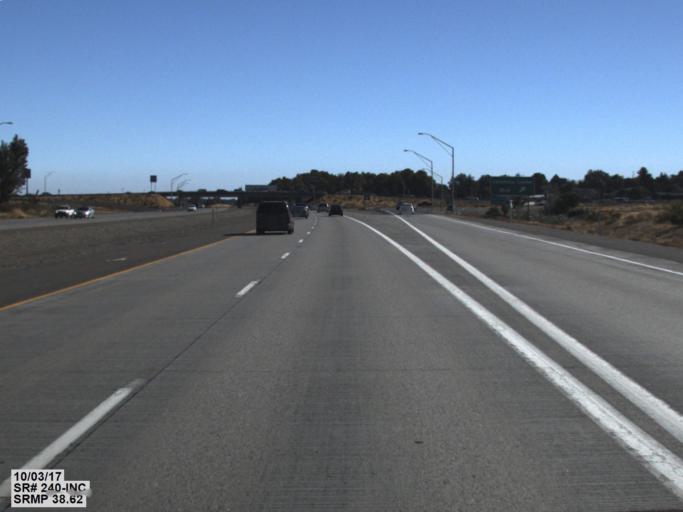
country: US
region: Washington
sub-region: Franklin County
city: West Pasco
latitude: 46.2329
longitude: -119.2293
